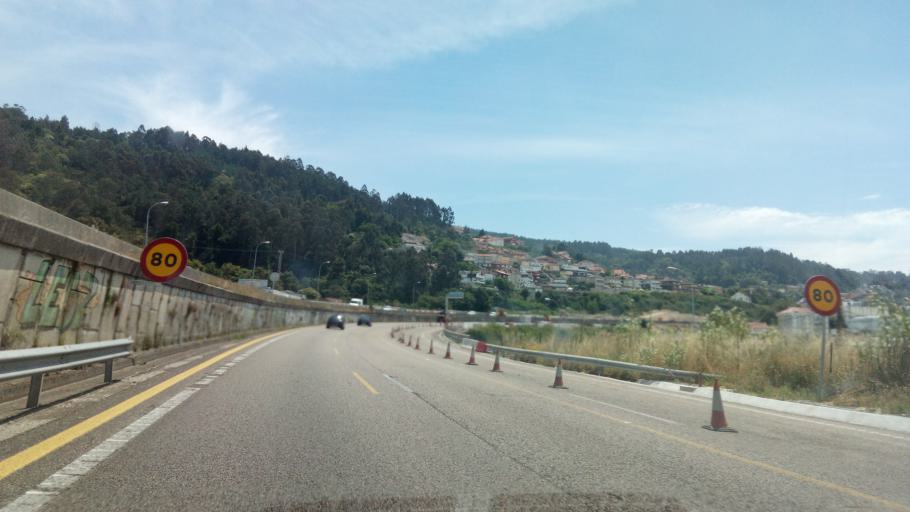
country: ES
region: Galicia
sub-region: Provincia de Pontevedra
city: Redondela
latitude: 42.2729
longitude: -8.6648
